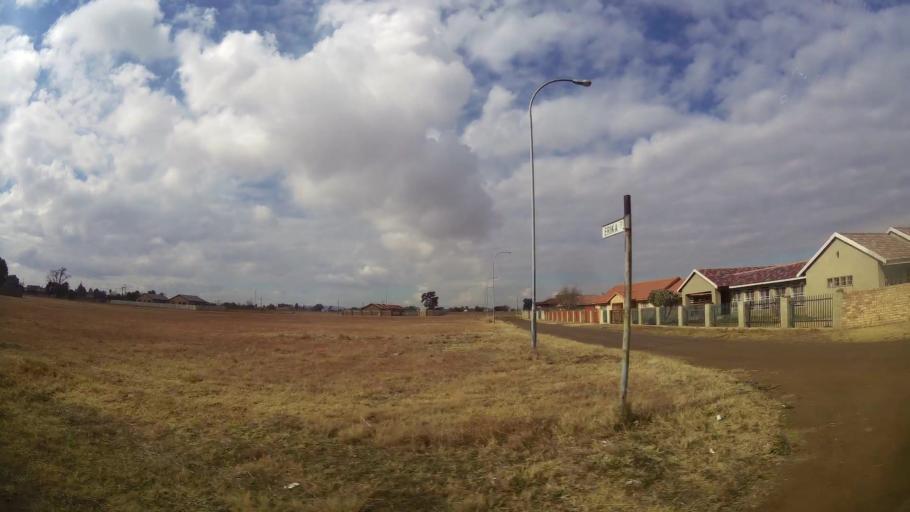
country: ZA
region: Gauteng
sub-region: Sedibeng District Municipality
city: Meyerton
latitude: -26.6104
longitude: 28.0487
